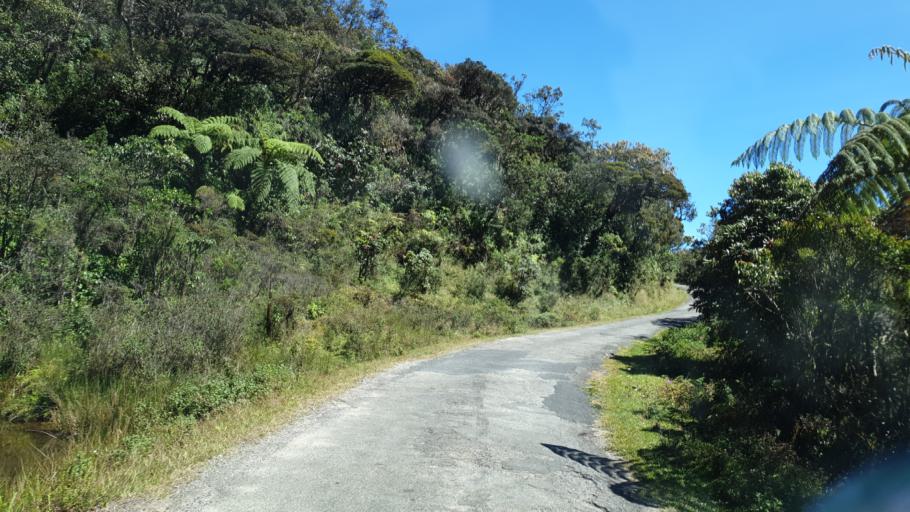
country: LK
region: Central
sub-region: Nuwara Eliya District
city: Nuwara Eliya
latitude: 6.8336
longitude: 80.8089
